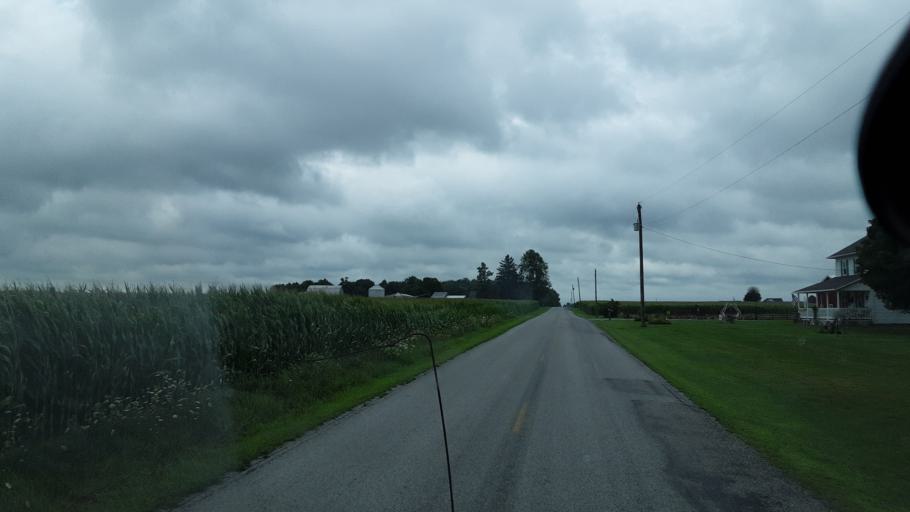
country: US
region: Indiana
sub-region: Wells County
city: Ossian
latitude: 40.9140
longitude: -85.1097
